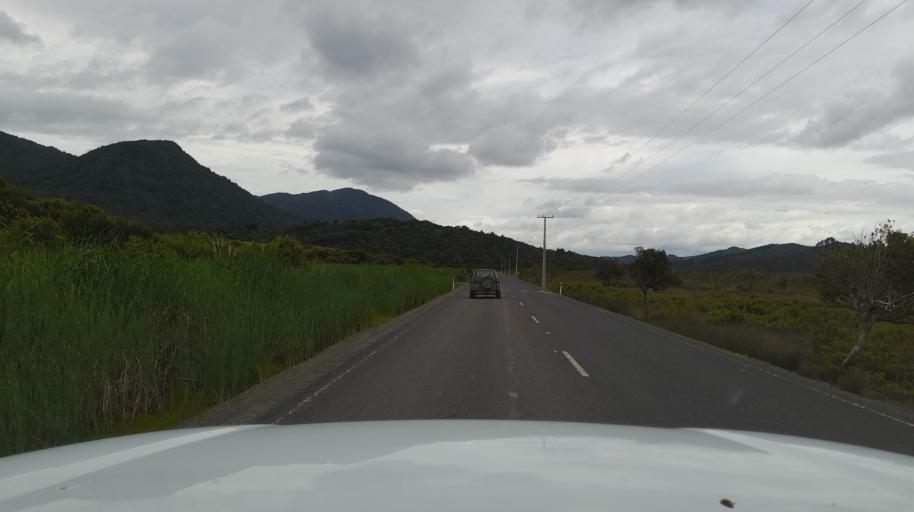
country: NZ
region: Northland
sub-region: Far North District
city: Kaitaia
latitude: -35.4071
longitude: 173.3825
